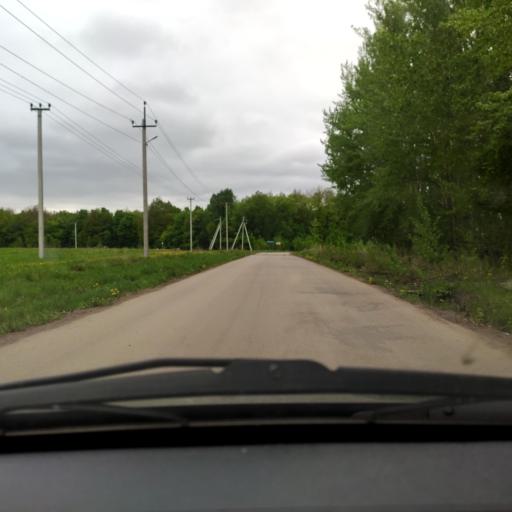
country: RU
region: Bashkortostan
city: Kabakovo
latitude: 54.6195
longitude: 56.1580
